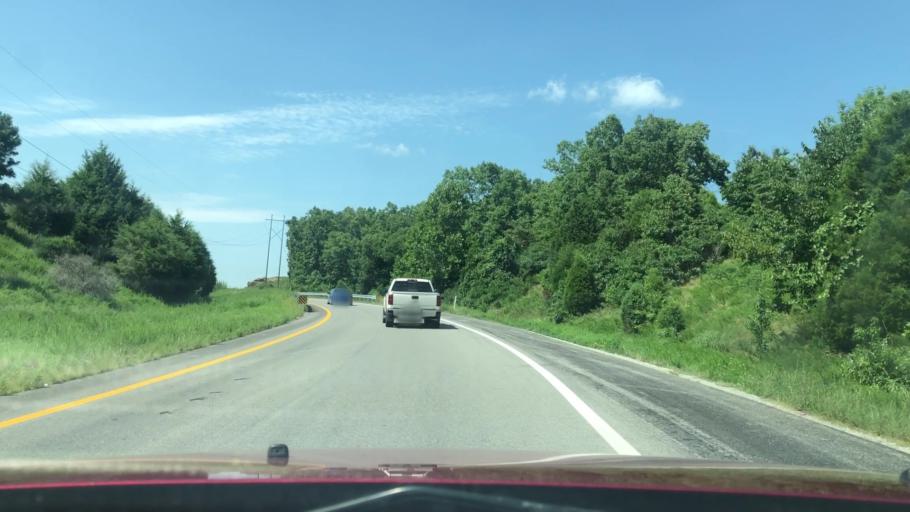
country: US
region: Missouri
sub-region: Taney County
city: Branson
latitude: 36.6759
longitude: -93.3155
